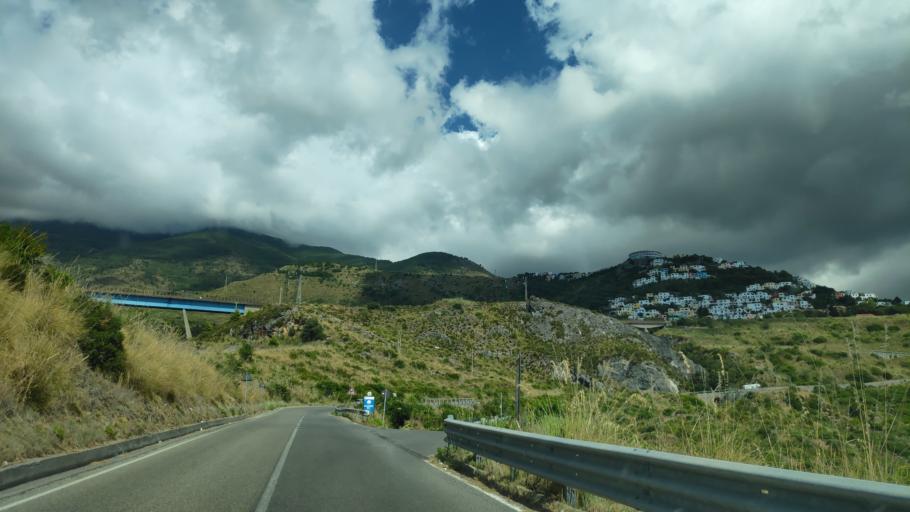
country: IT
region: Calabria
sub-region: Provincia di Cosenza
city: San Nicola Arcella
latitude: 39.8684
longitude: 15.7918
